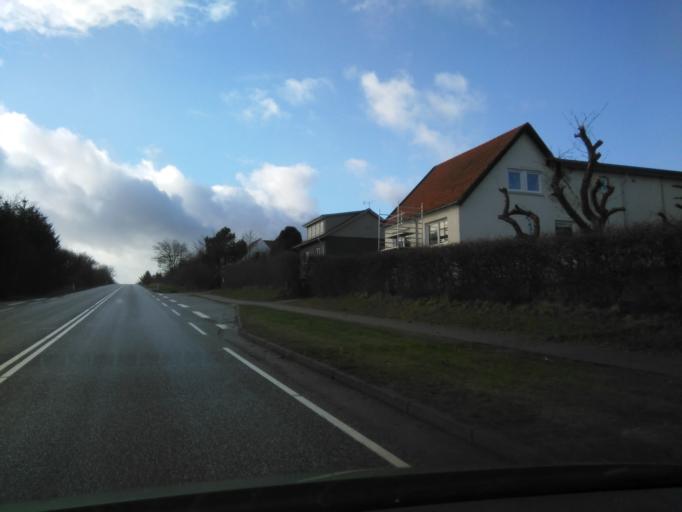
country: DK
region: Central Jutland
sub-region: Skanderborg Kommune
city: Skanderborg
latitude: 56.0233
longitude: 9.8966
